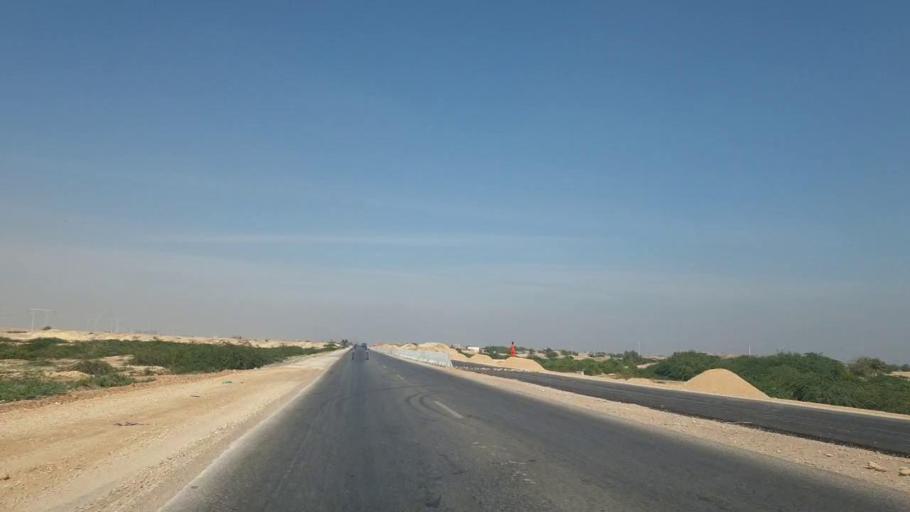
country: PK
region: Sindh
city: Matiari
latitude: 25.6670
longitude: 68.2955
